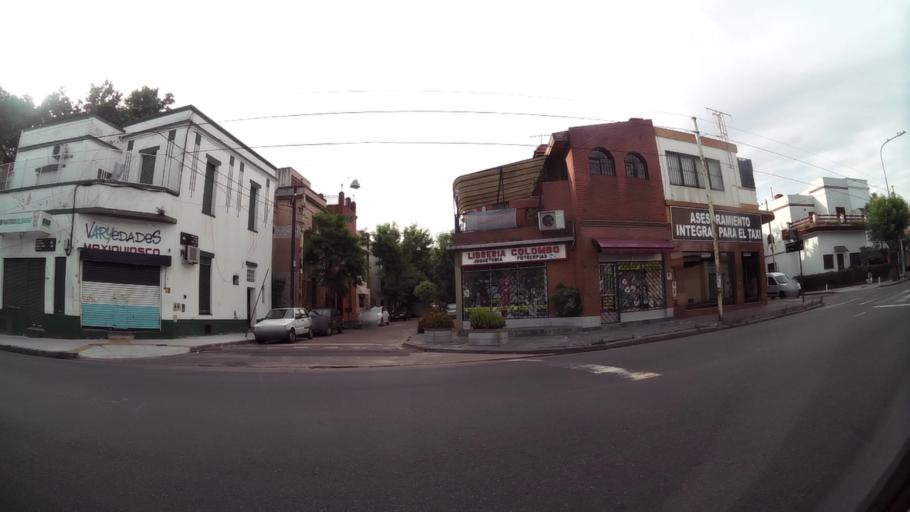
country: AR
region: Buenos Aires F.D.
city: Villa Santa Rita
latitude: -34.6394
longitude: -58.4543
